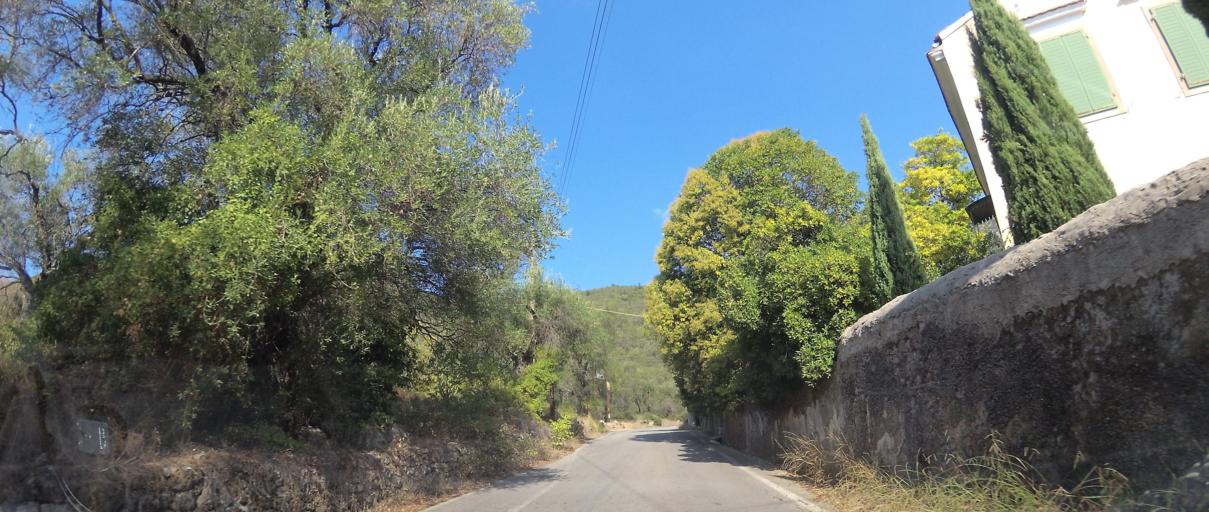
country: GR
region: Ionian Islands
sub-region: Nomos Kerkyras
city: Kontokali
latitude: 39.7142
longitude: 19.8459
